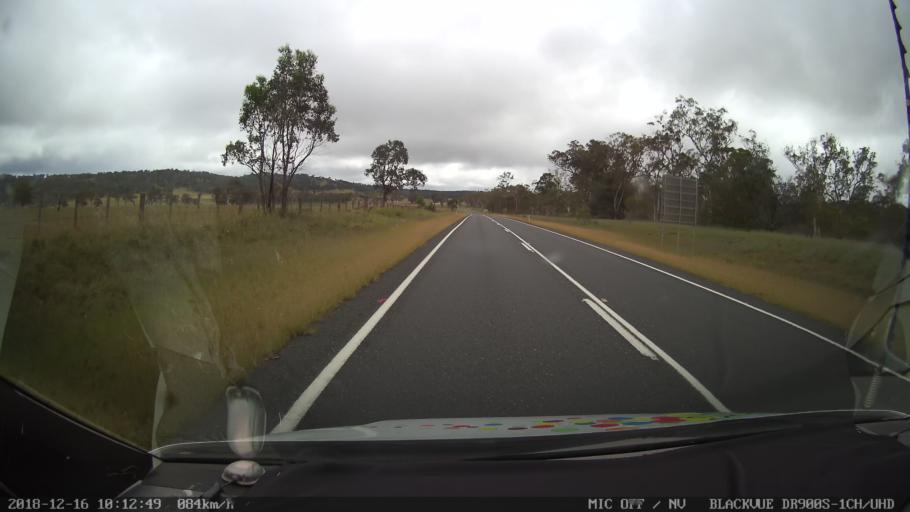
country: AU
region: New South Wales
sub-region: Glen Innes Severn
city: Glen Innes
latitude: -29.3027
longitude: 151.9451
